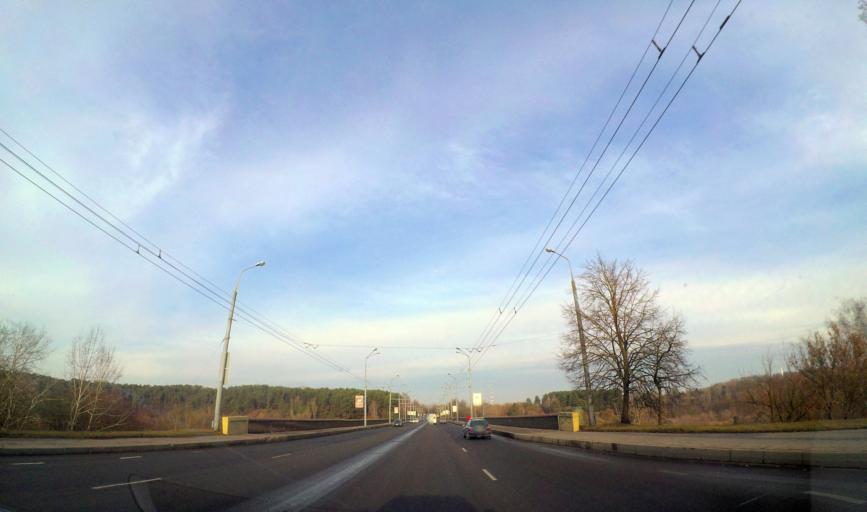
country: BY
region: Grodnenskaya
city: Hrodna
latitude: 53.6777
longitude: 23.8058
